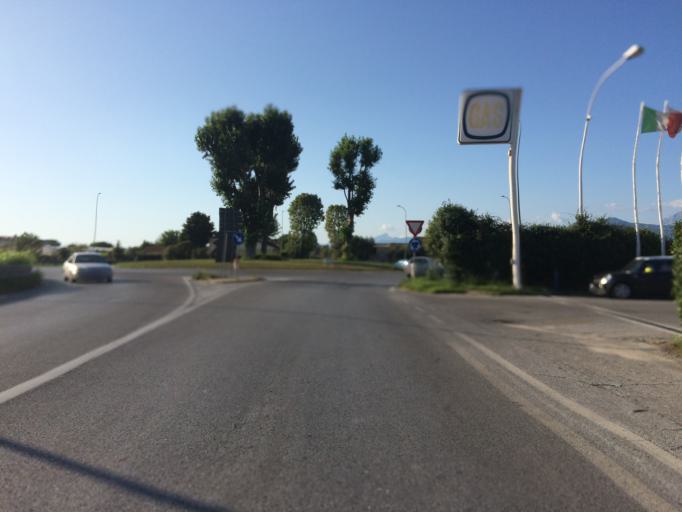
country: IT
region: Tuscany
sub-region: Provincia di Lucca
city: Torre del Lago Puccini
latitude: 43.8345
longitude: 10.2876
